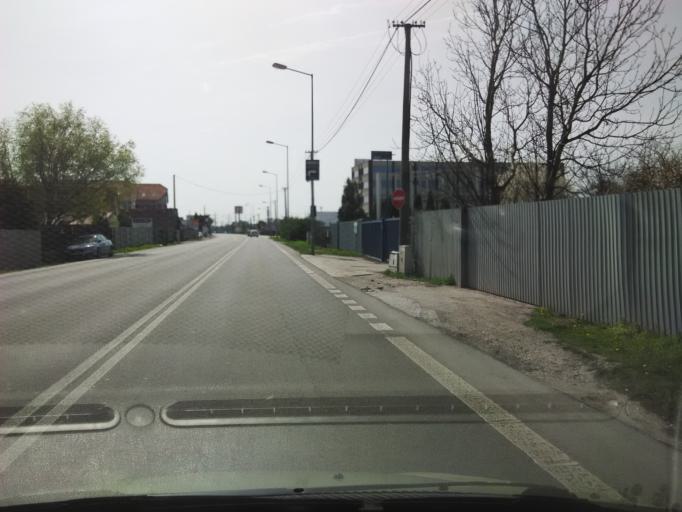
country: SK
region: Bratislavsky
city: Dunajska Luzna
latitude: 48.1353
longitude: 17.1935
